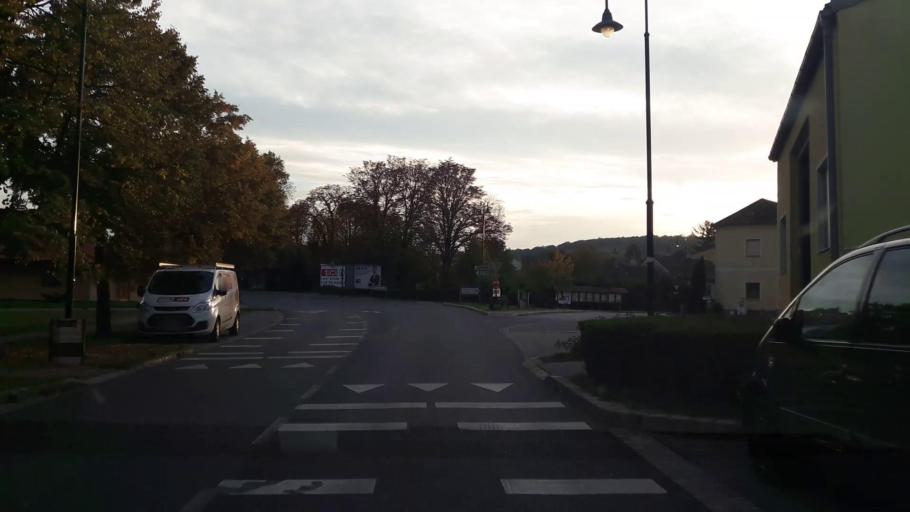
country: AT
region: Lower Austria
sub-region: Politischer Bezirk Korneuburg
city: Grossrussbach
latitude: 48.4610
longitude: 16.3739
